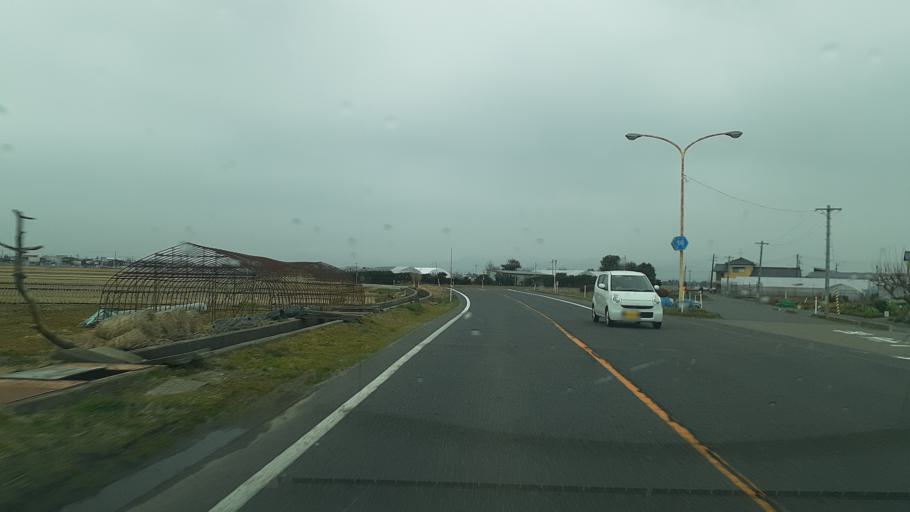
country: JP
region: Niigata
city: Kameda-honcho
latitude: 37.8631
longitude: 139.0682
